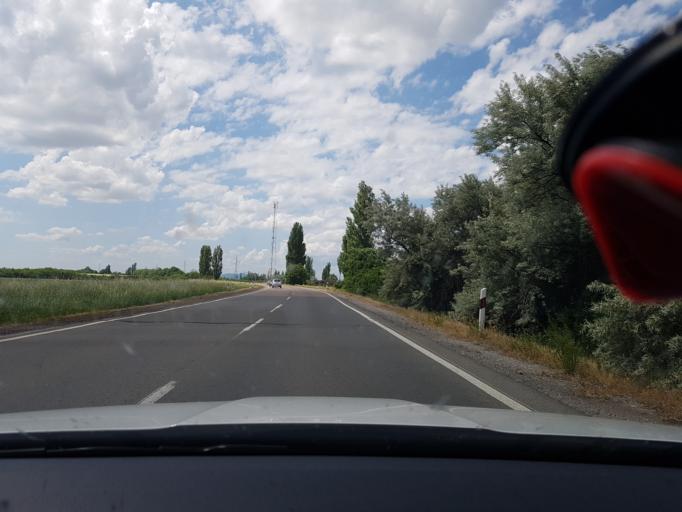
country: HU
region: Heves
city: Kompolt
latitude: 47.7635
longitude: 20.2246
